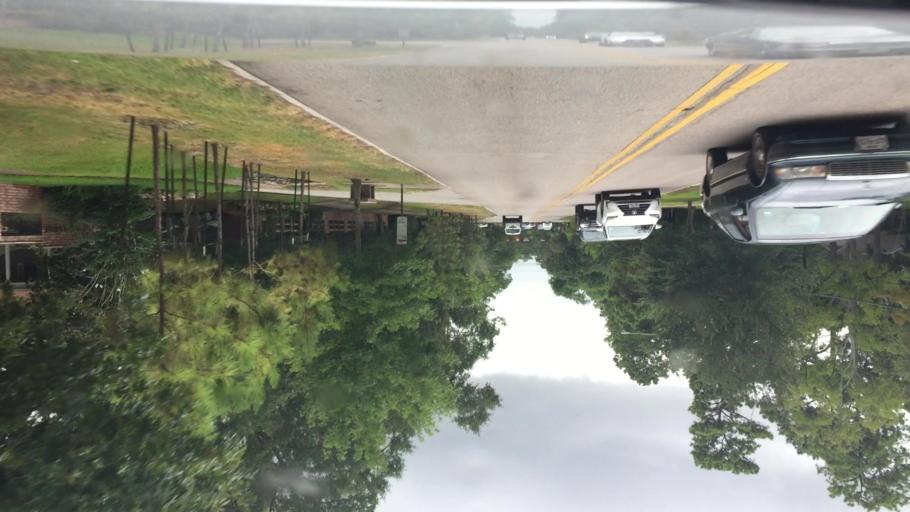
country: US
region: Texas
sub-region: Harris County
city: Hunters Creek Village
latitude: 29.7645
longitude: -95.5035
